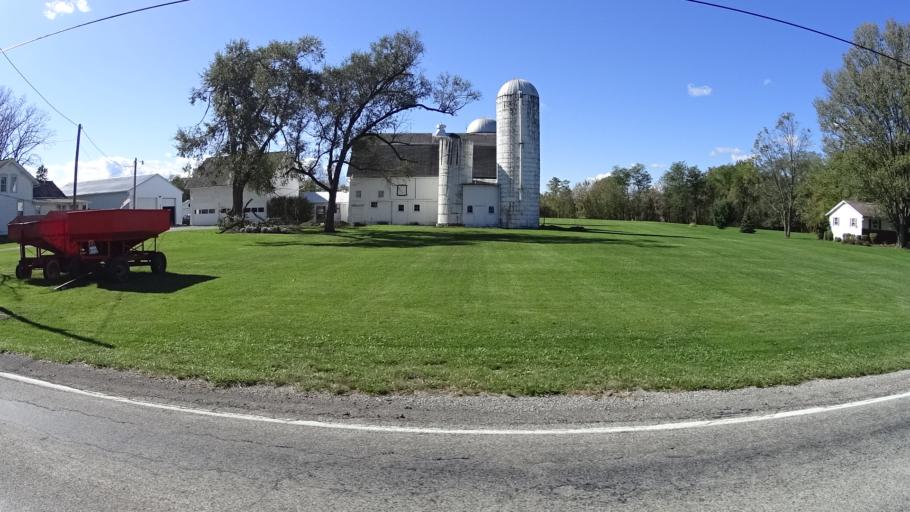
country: US
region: Ohio
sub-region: Lorain County
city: Grafton
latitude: 41.3065
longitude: -82.0881
